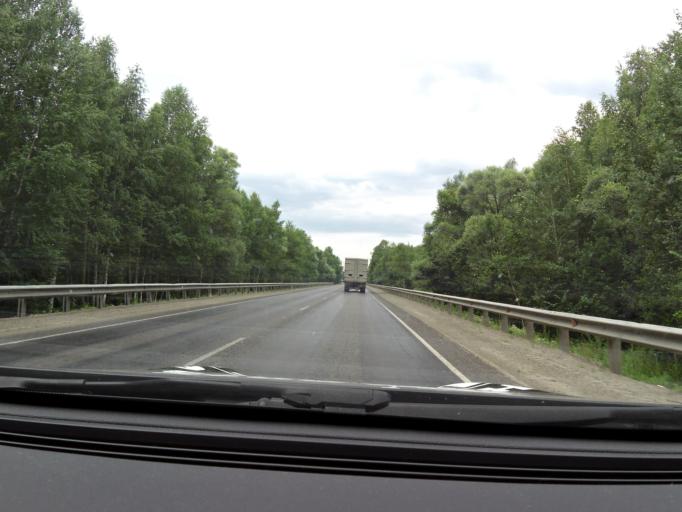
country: RU
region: Bashkortostan
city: Ulu-Telyak
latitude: 54.8316
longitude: 56.9514
